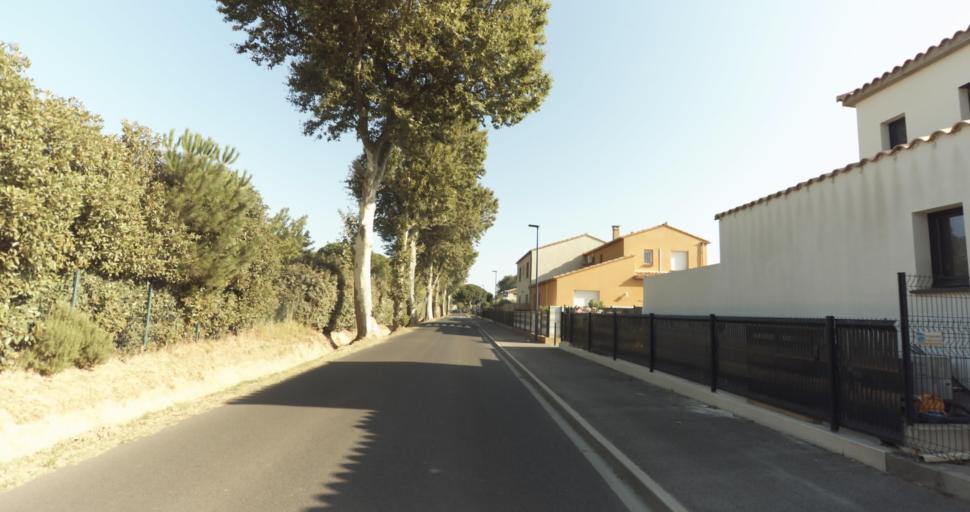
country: FR
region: Languedoc-Roussillon
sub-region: Departement des Pyrenees-Orientales
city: Alenya
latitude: 42.6364
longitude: 2.9865
